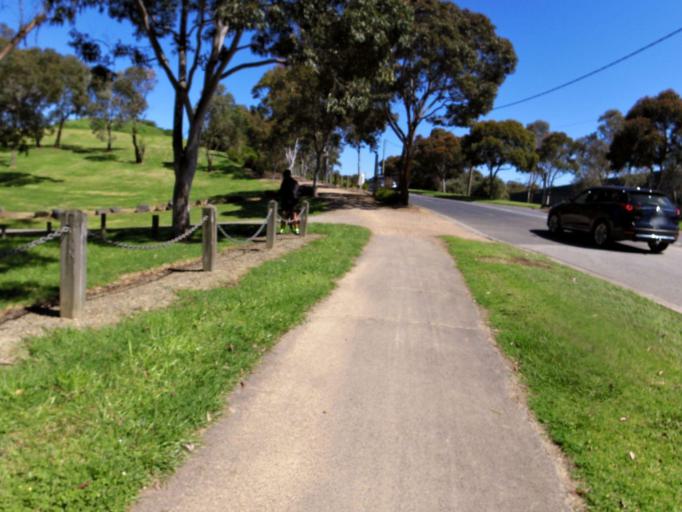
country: AU
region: Victoria
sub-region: Whitehorse
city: Vermont South
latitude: -37.8593
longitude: 145.1979
